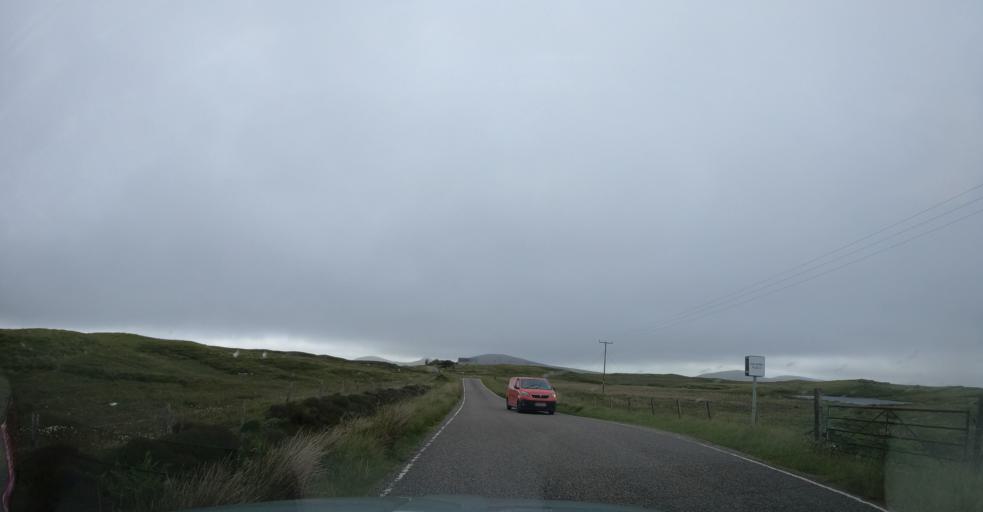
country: GB
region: Scotland
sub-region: Eilean Siar
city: Isle of North Uist
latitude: 57.6110
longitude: -7.1831
